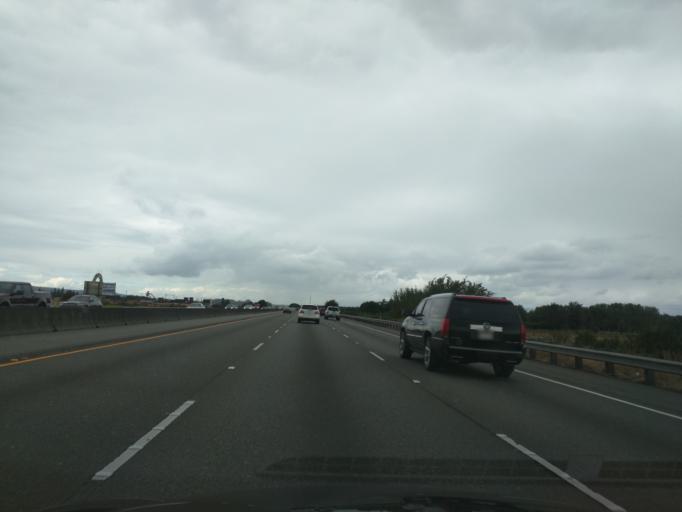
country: US
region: Washington
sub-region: Snohomish County
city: Marysville
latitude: 48.0143
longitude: -122.1746
